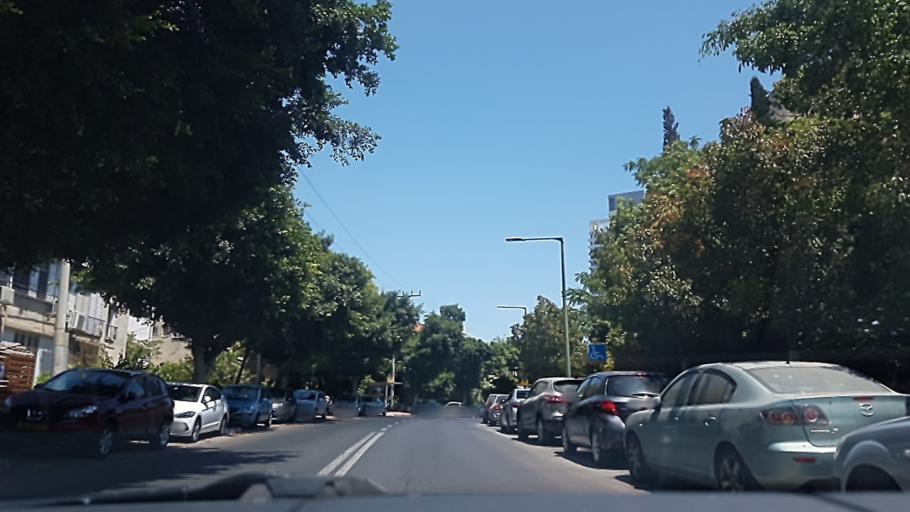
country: IL
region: Tel Aviv
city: Ramat Gan
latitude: 32.0869
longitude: 34.8074
